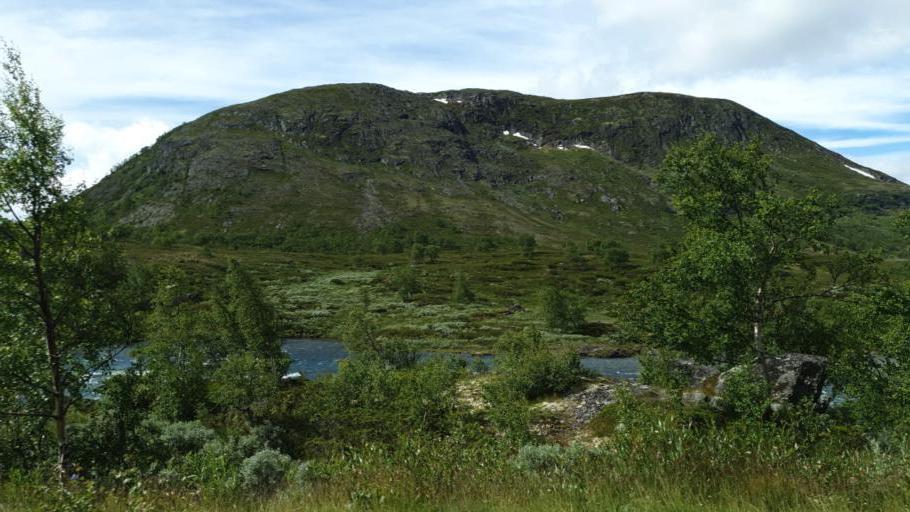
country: NO
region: Oppland
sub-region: Lom
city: Fossbergom
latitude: 61.4910
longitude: 8.8176
